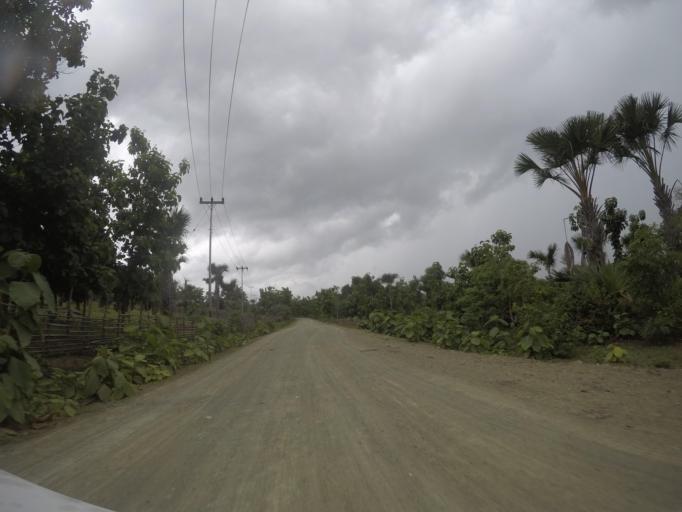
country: TL
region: Bobonaro
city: Maliana
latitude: -8.8540
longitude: 125.0819
